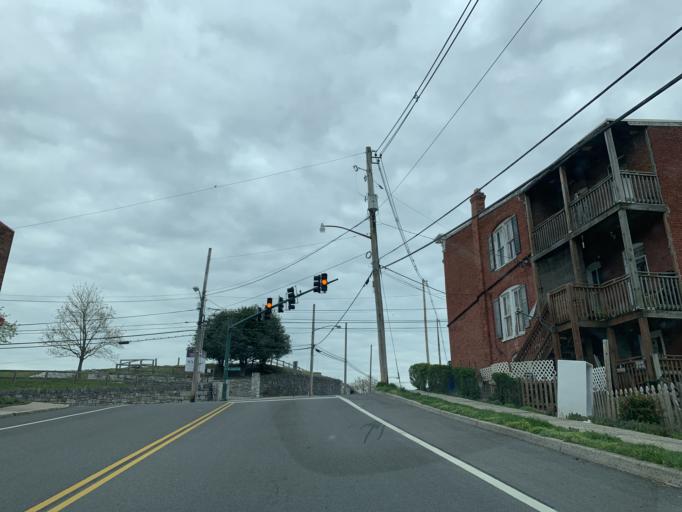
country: US
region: Maryland
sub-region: Washington County
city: Hagerstown
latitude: 39.6378
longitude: -77.7148
